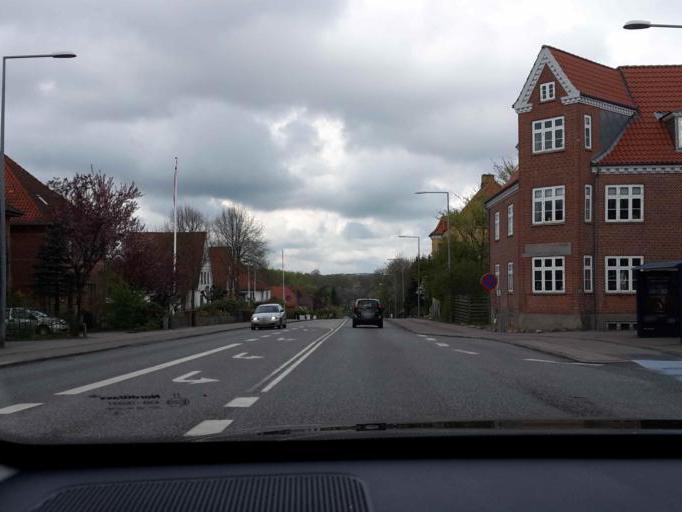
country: DK
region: South Denmark
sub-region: Vejle Kommune
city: Vejle
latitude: 55.6951
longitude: 9.5421
